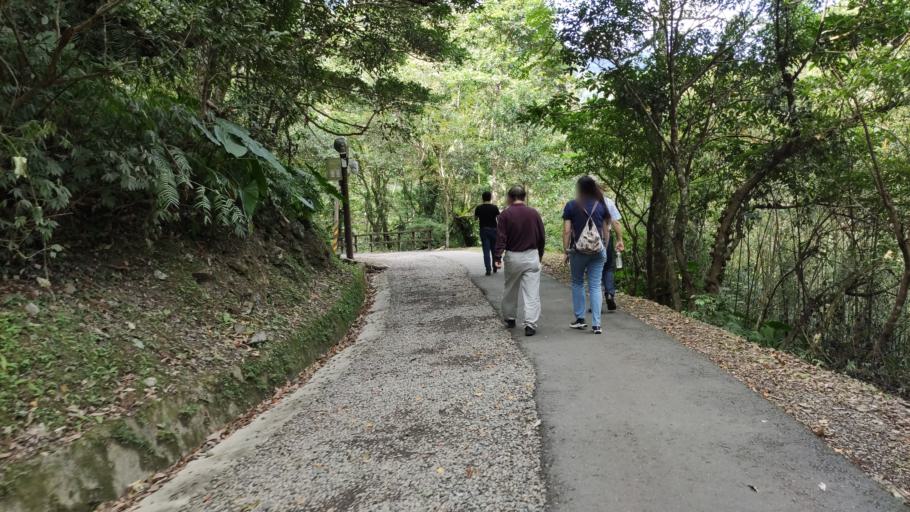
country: TW
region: Taiwan
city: Daxi
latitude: 24.8283
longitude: 121.4459
